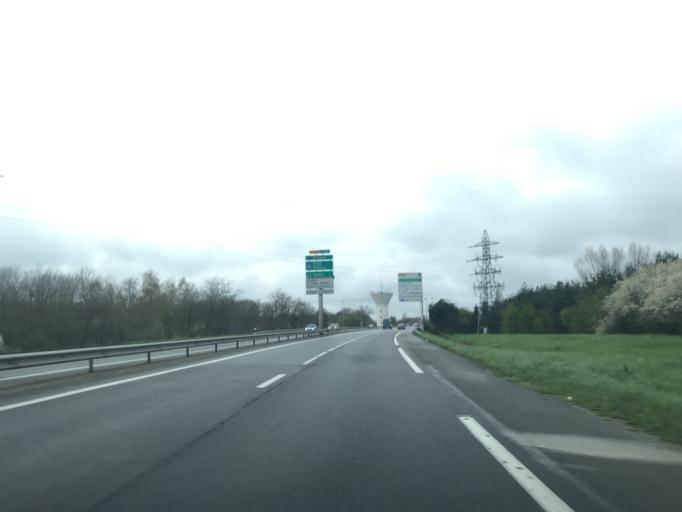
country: FR
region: Centre
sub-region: Departement du Loiret
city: Saint-Jean-de-Braye
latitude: 47.9212
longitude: 1.9975
